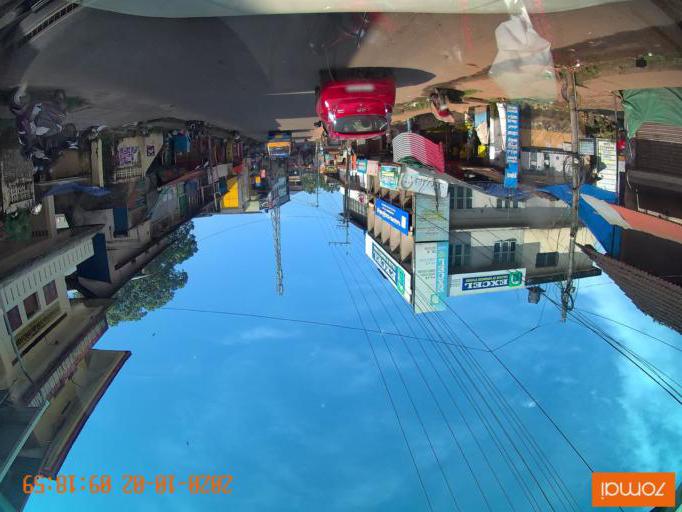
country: IN
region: Kerala
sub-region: Kozhikode
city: Naduvannur
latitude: 11.5609
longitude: 75.7578
